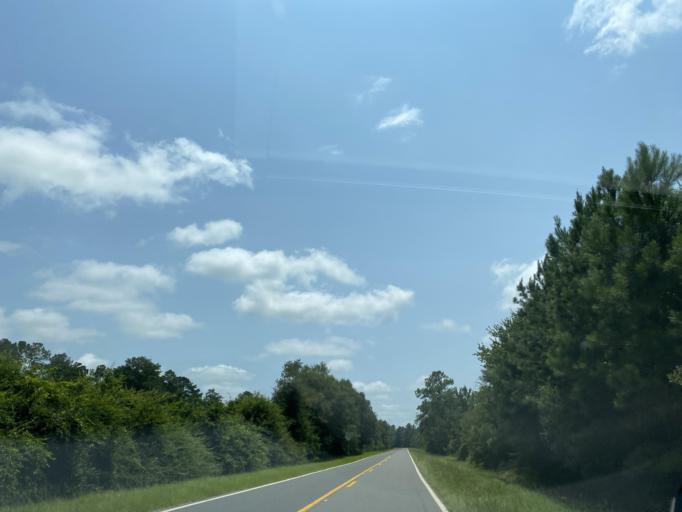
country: US
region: Georgia
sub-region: Telfair County
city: Lumber City
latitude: 31.9621
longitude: -82.7005
